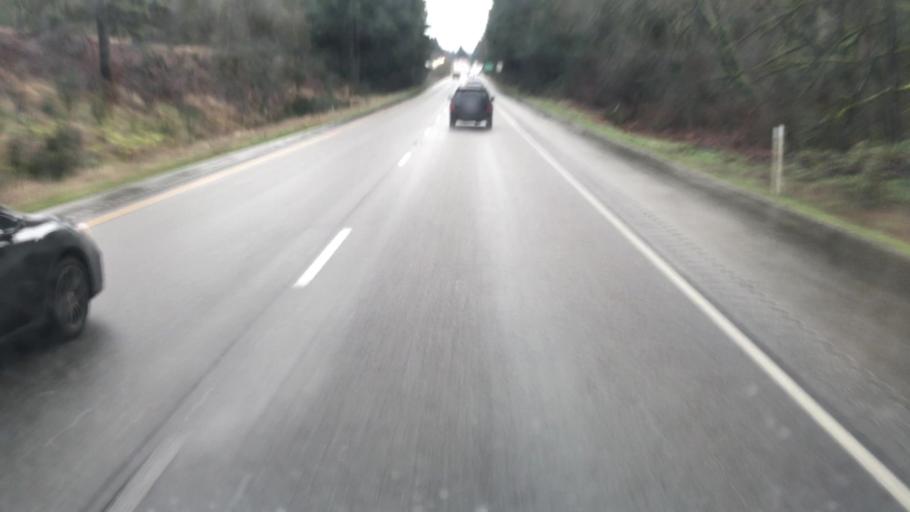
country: US
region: Washington
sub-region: Kitsap County
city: Burley
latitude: 47.4411
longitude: -122.6228
